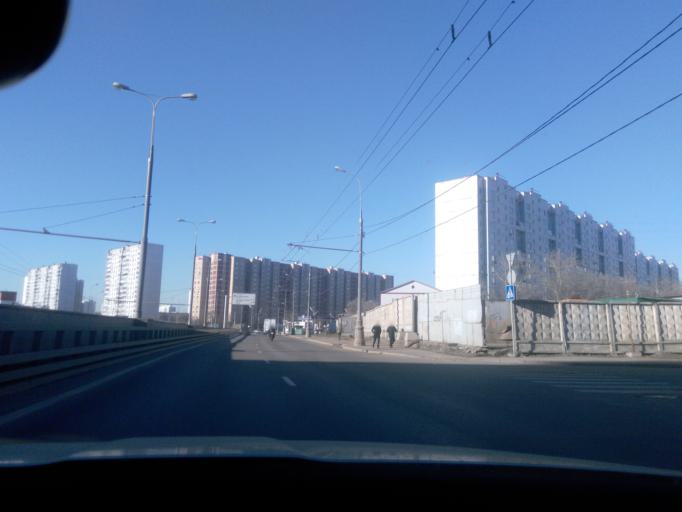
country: RU
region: Moskovskaya
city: Khoroshevo-Mnevniki
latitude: 55.7736
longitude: 37.4978
